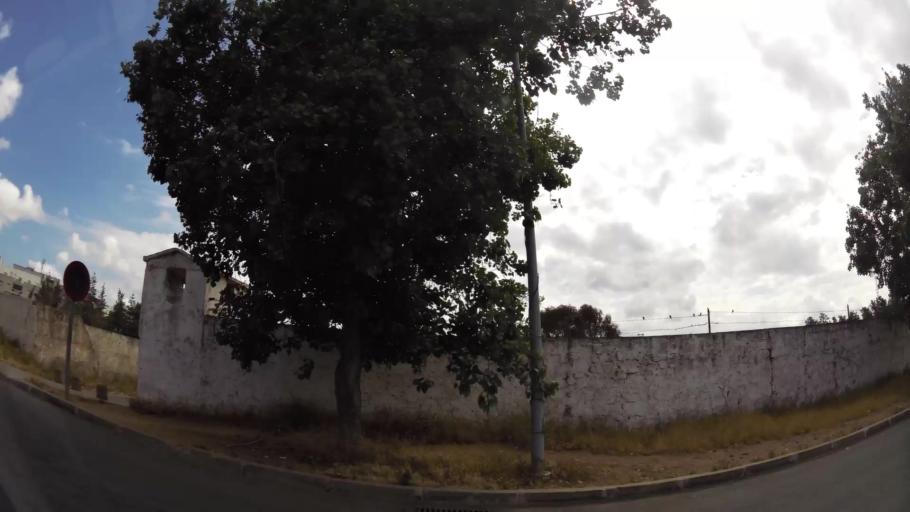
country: MA
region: Gharb-Chrarda-Beni Hssen
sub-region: Kenitra Province
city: Kenitra
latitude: 34.2509
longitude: -6.5944
